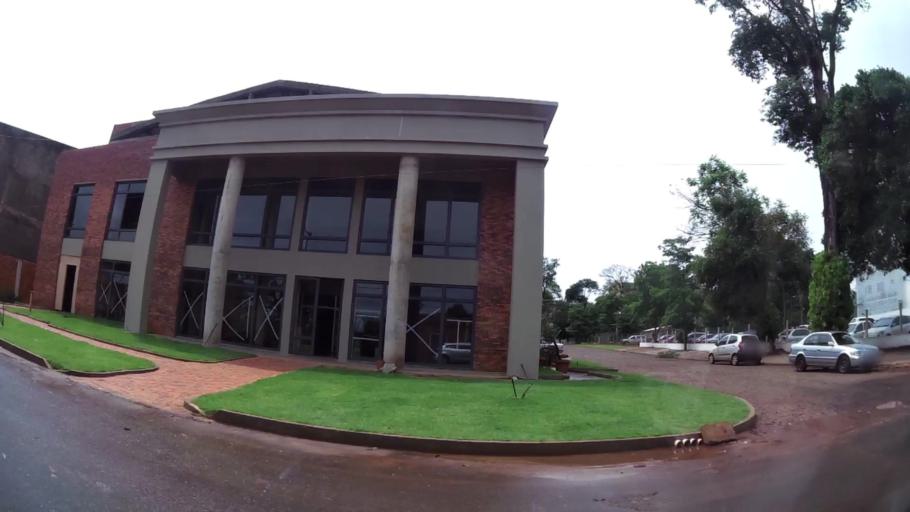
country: PY
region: Alto Parana
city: Ciudad del Este
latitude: -25.5135
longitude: -54.6449
